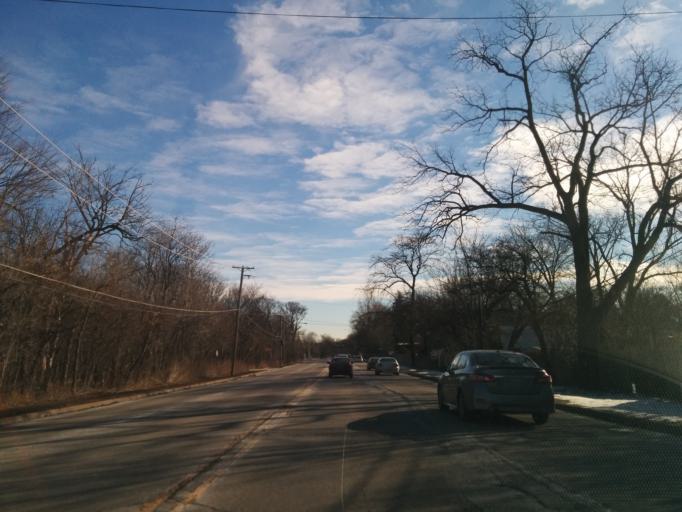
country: US
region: Illinois
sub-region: DuPage County
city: Glen Ellyn
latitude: 41.8900
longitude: -88.0601
